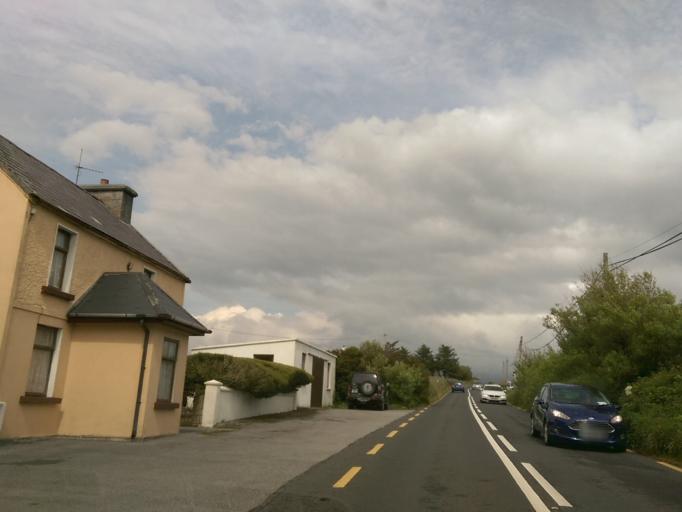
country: IE
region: Connaught
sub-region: County Galway
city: Bearna
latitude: 53.0505
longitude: -9.2274
